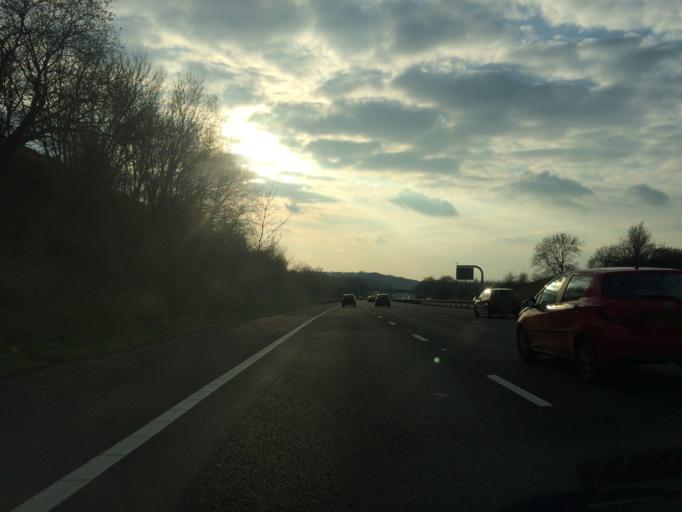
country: GB
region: England
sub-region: Borough of Swindon
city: Wanborough
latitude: 51.5255
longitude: -1.7094
